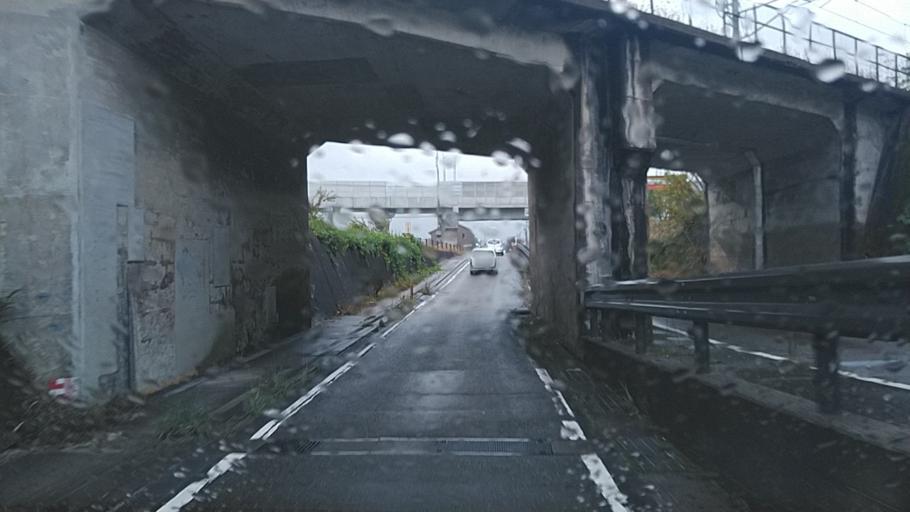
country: JP
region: Ishikawa
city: Komatsu
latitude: 36.3235
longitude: 136.3578
